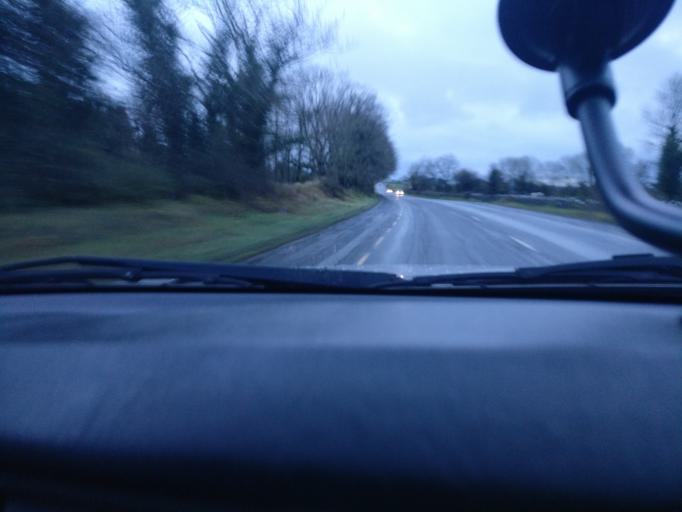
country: IE
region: Connaught
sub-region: County Galway
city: Loughrea
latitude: 53.2385
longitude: -8.4517
